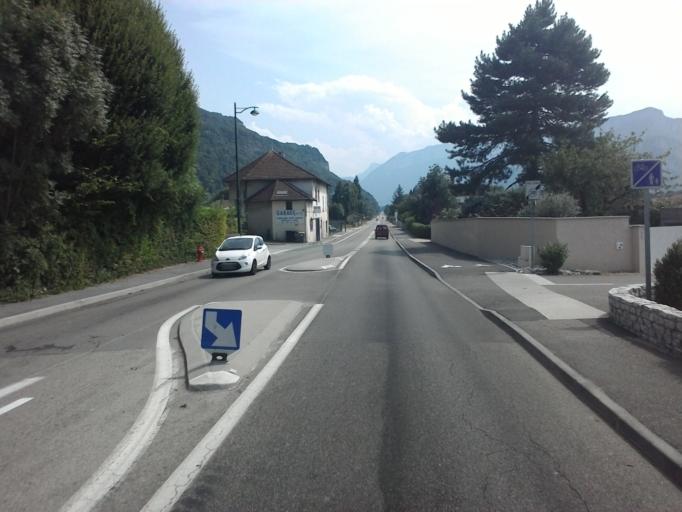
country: FR
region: Rhone-Alpes
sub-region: Departement de l'Isere
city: La Buisse
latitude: 45.3334
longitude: 5.6207
